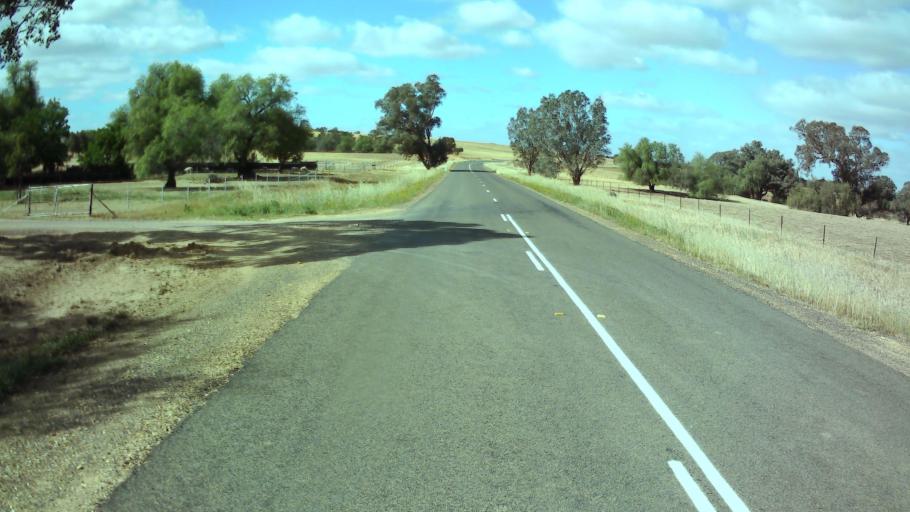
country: AU
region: New South Wales
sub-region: Weddin
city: Grenfell
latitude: -33.9728
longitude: 148.4258
